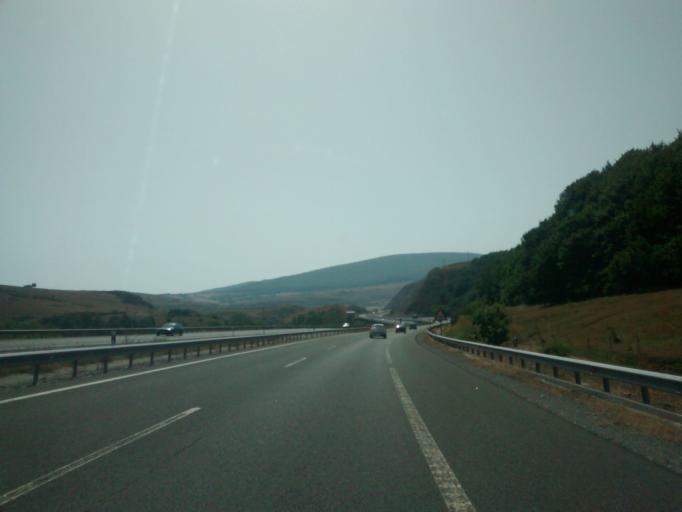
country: ES
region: Cantabria
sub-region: Provincia de Cantabria
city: Villaescusa
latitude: 42.9524
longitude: -4.1473
